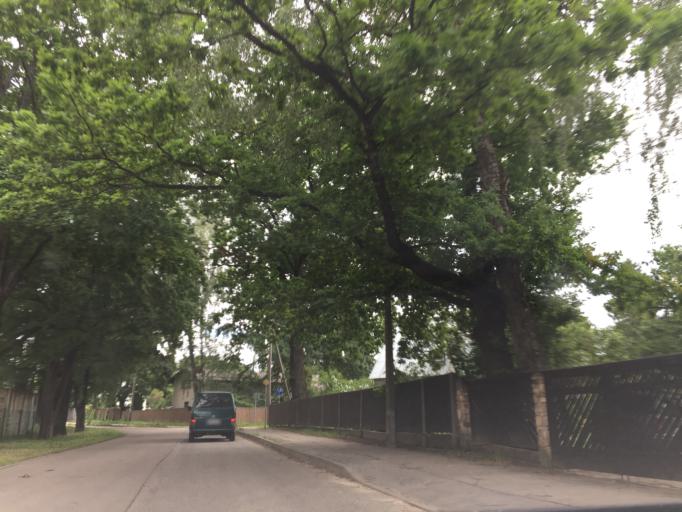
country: LV
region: Marupe
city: Marupe
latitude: 56.9411
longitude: 24.0296
